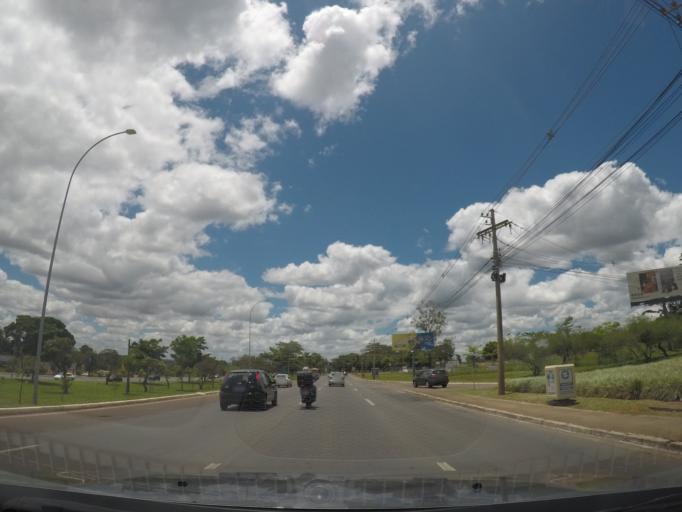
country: BR
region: Federal District
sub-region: Brasilia
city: Brasilia
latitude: -15.7222
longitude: -47.8870
